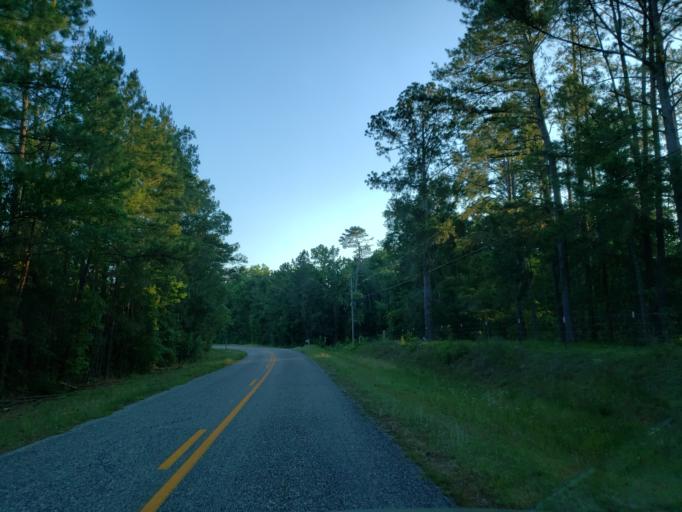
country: US
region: Georgia
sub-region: Crisp County
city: Cordele
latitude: 32.0206
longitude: -83.7530
